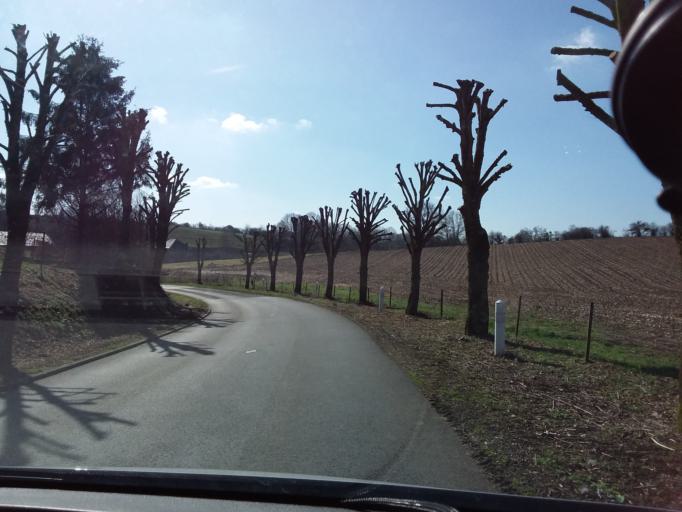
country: FR
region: Picardie
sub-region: Departement de l'Aisne
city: Hirson
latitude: 49.8830
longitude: 4.0957
